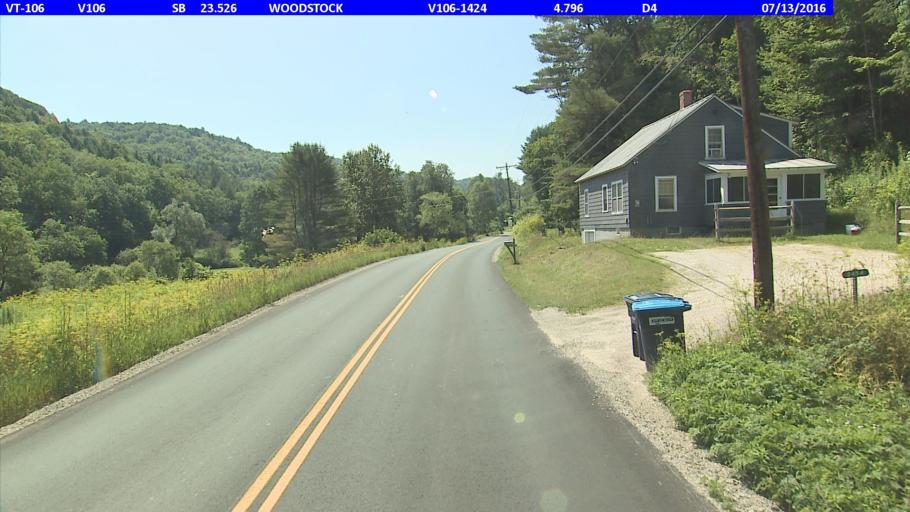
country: US
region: Vermont
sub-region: Windsor County
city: Woodstock
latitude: 43.5899
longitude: -72.5159
